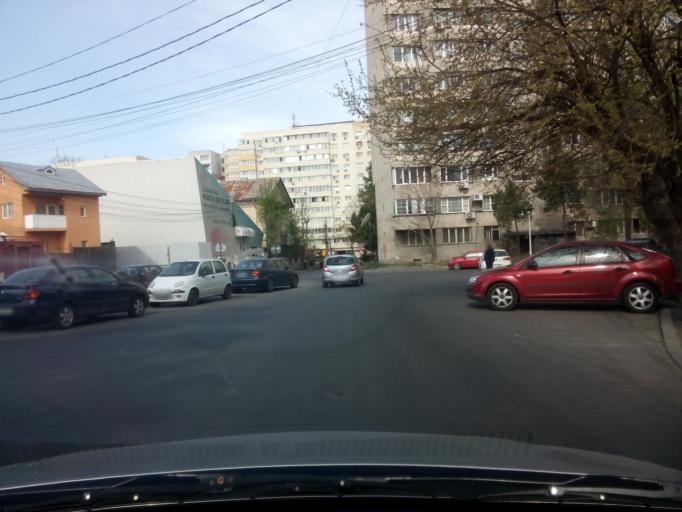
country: RO
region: Bucuresti
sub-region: Municipiul Bucuresti
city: Bucharest
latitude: 44.4549
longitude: 26.1303
